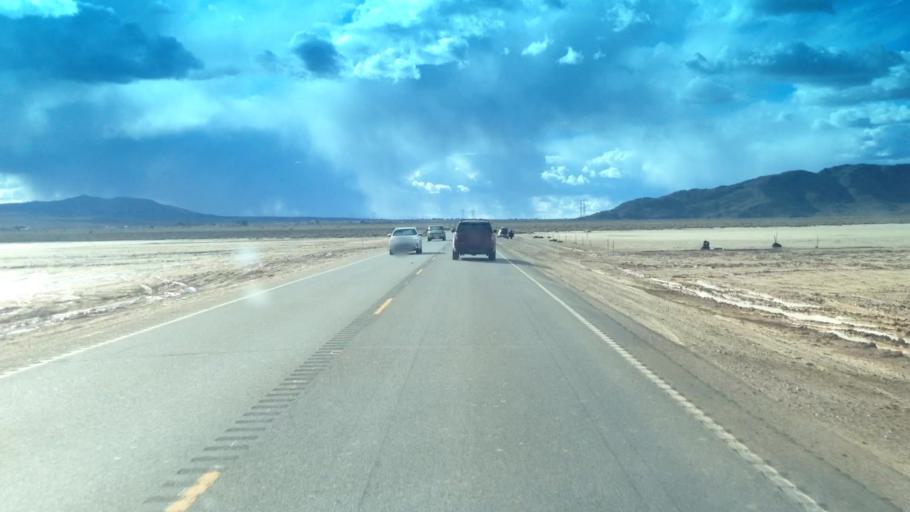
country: US
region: California
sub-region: San Bernardino County
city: Lucerne Valley
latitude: 34.4508
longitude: -117.0191
